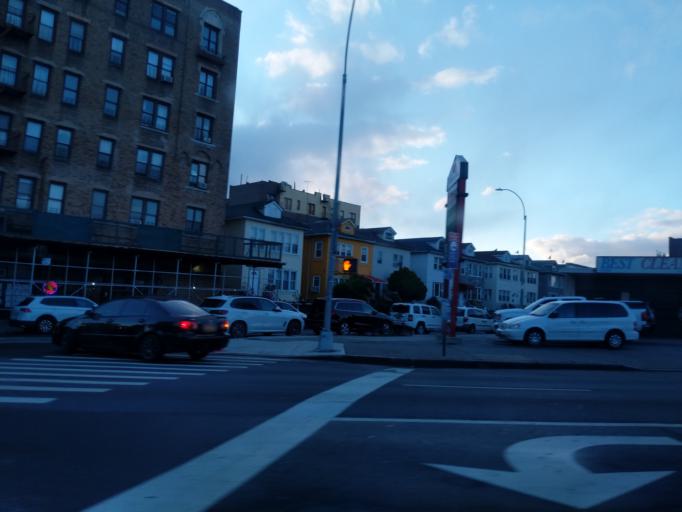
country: US
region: New York
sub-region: Bronx
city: The Bronx
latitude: 40.8634
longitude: -73.8652
